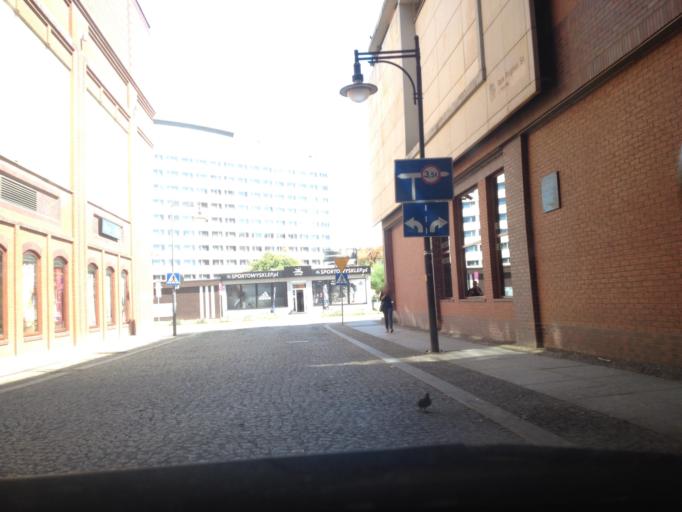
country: PL
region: Lower Silesian Voivodeship
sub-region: Legnica
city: Legnica
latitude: 51.2103
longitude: 16.1636
